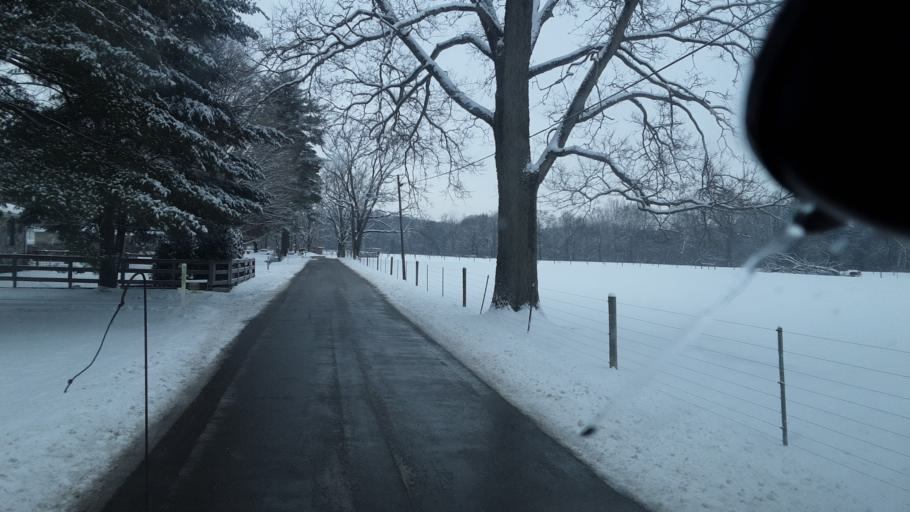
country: US
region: Ohio
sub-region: Licking County
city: Granville
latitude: 40.0634
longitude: -82.5004
